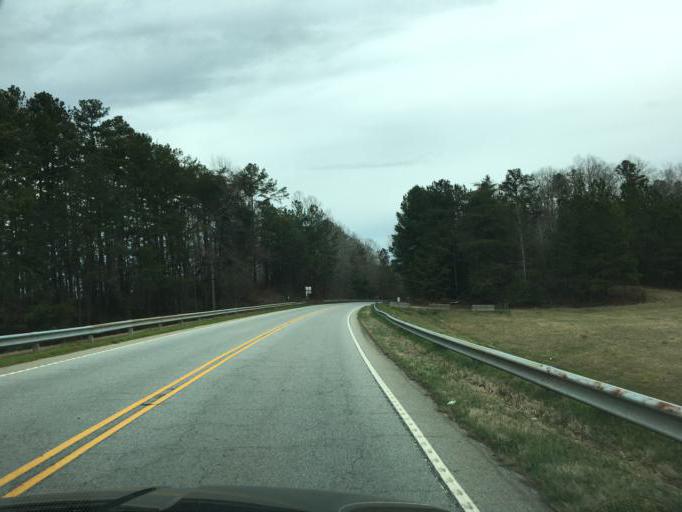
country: US
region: South Carolina
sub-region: Oconee County
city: Utica
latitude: 34.7469
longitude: -82.9084
